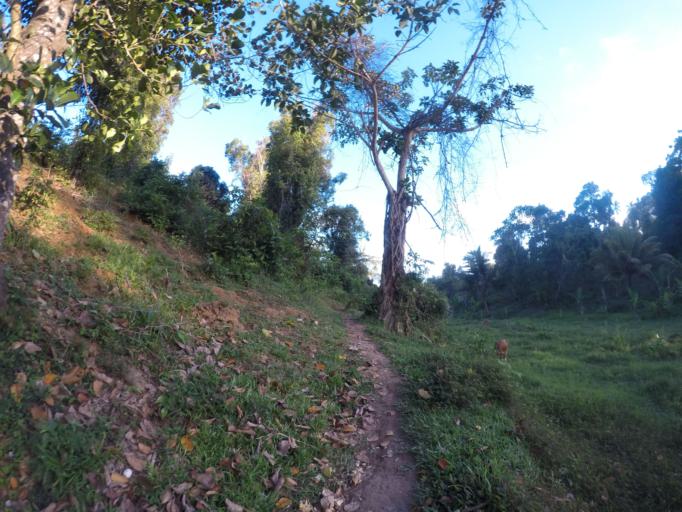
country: TZ
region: Pemba South
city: Mtambile
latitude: -5.3778
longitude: 39.7048
